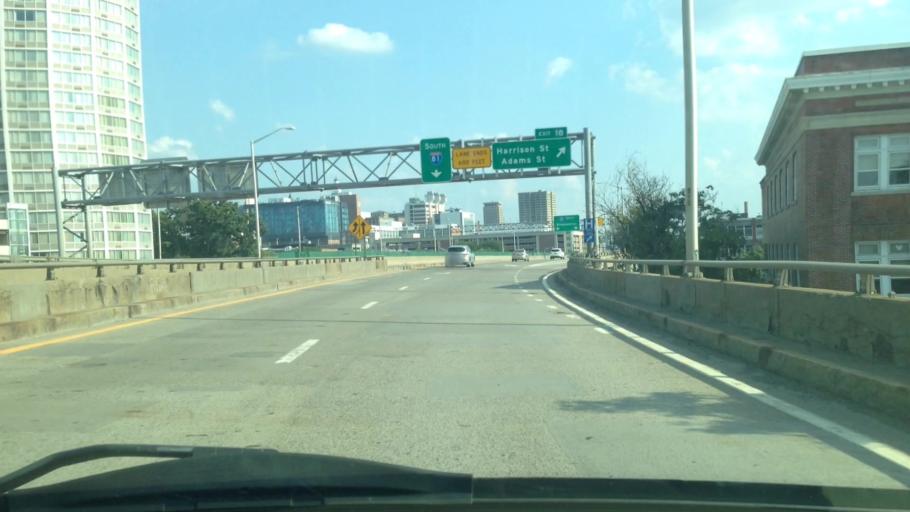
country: US
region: New York
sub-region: Onondaga County
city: Syracuse
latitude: 43.0487
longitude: -76.1429
